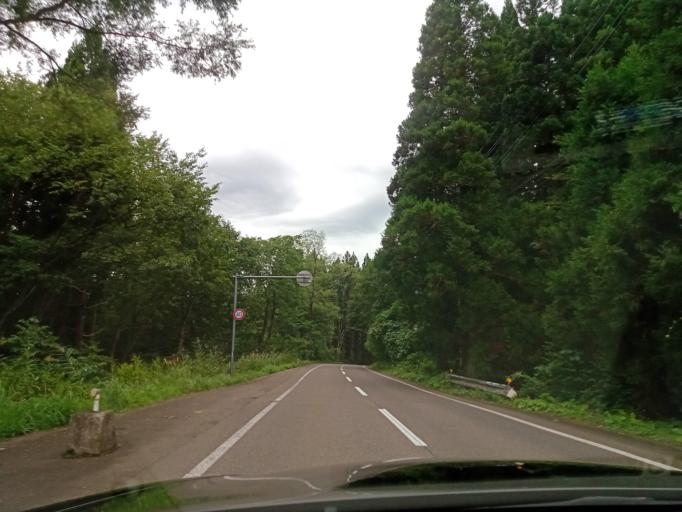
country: JP
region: Niigata
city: Arai
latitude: 36.8790
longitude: 138.1847
